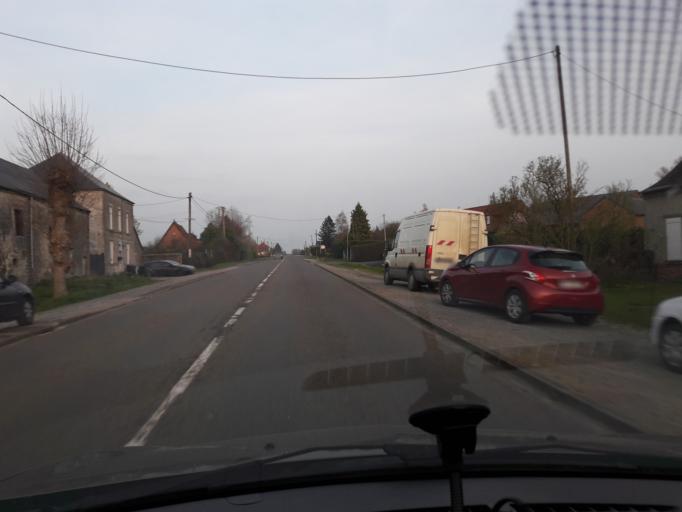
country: FR
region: Nord-Pas-de-Calais
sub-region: Departement du Nord
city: Marpent
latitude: 50.2533
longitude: 4.0816
